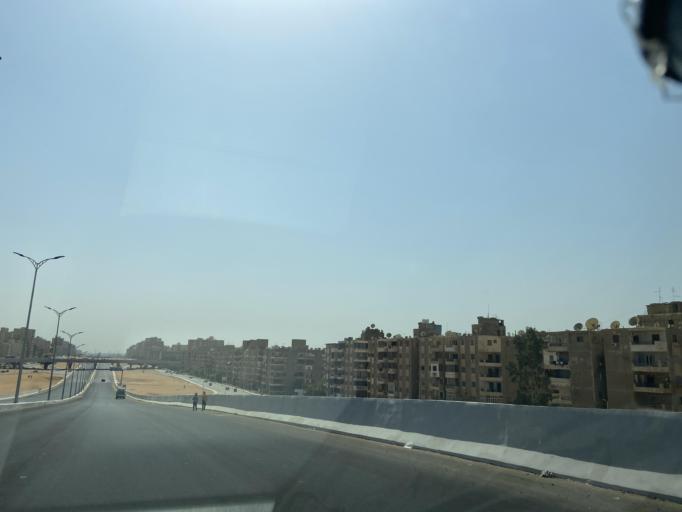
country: EG
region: Muhafazat al Qahirah
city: Cairo
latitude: 30.0619
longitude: 31.3792
